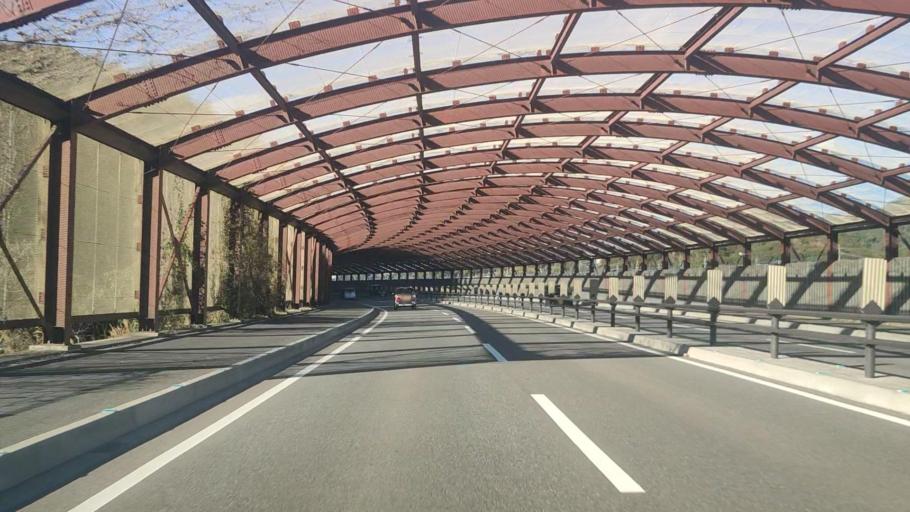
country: JP
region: Fukuoka
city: Dazaifu
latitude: 33.5097
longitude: 130.5500
